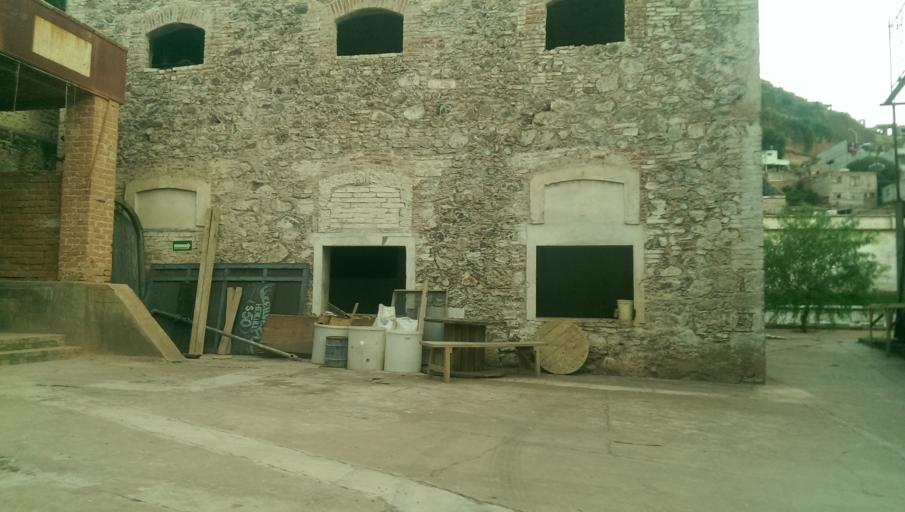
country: MX
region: Queretaro
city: La Canada
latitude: 20.6001
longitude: -100.3547
